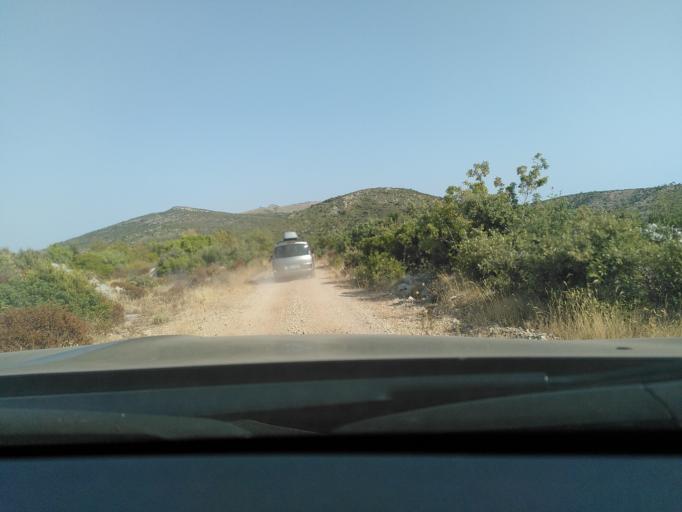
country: HR
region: Splitsko-Dalmatinska
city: Stari Grad
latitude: 43.1626
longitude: 16.5520
